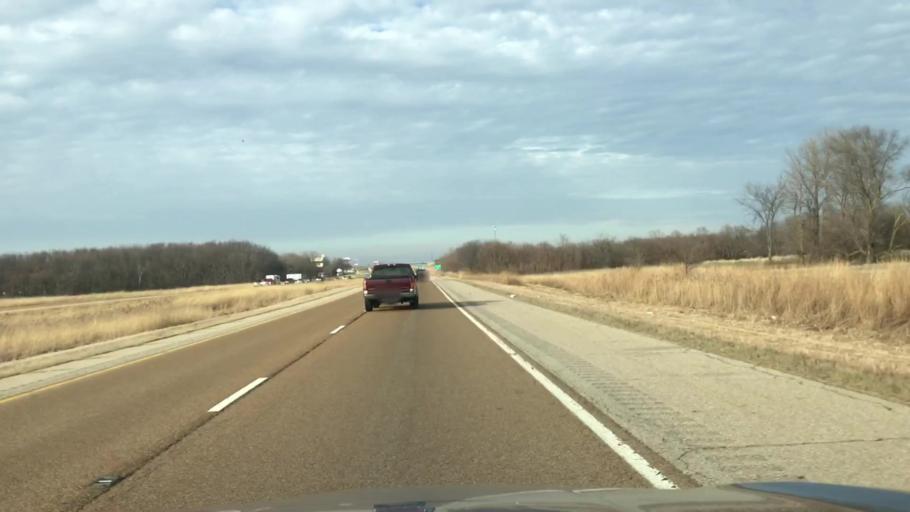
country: US
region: Illinois
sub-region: Montgomery County
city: Raymond
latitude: 39.4318
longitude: -89.6435
